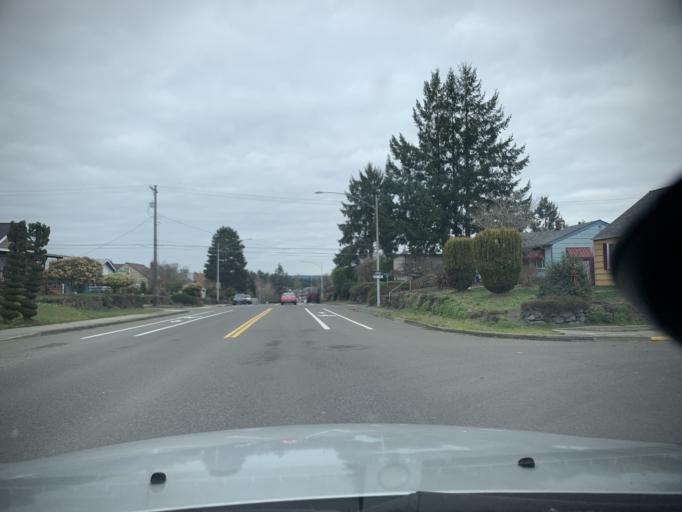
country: US
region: Washington
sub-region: Pierce County
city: Fircrest
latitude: 47.2960
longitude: -122.5210
